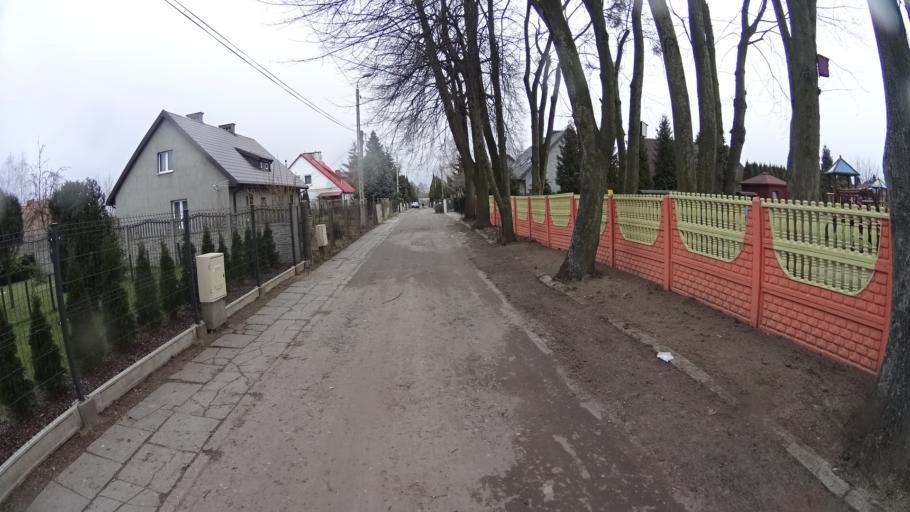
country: PL
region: Masovian Voivodeship
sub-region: Powiat warszawski zachodni
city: Blonie
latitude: 52.2167
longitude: 20.6481
